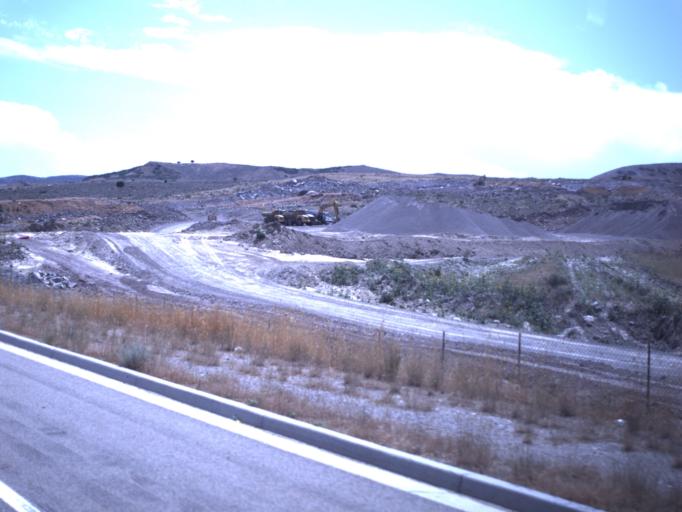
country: US
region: Utah
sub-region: Salt Lake County
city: Herriman
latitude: 40.4830
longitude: -111.9914
